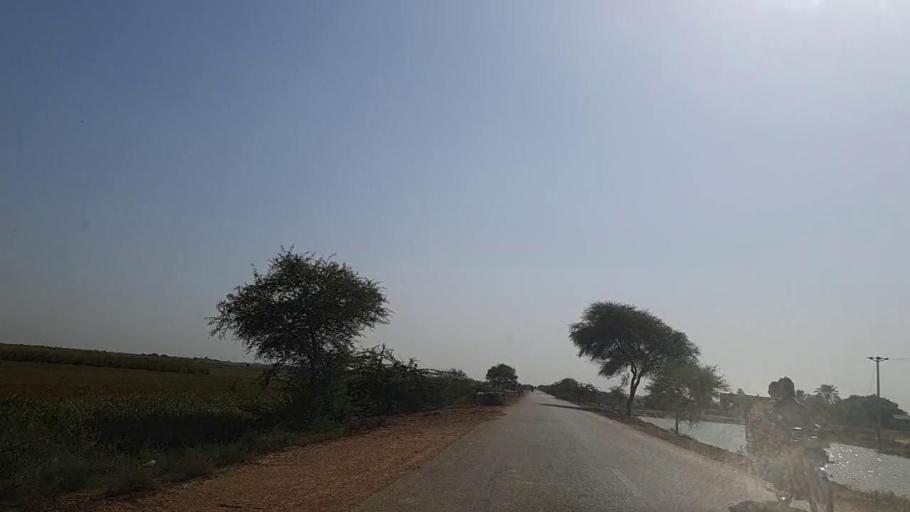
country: PK
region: Sindh
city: Mirpur Batoro
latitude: 24.5924
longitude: 68.2924
